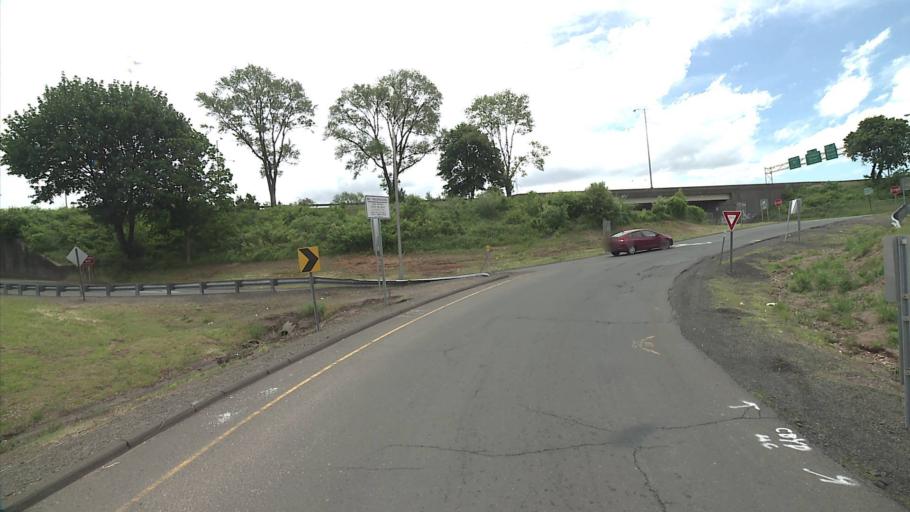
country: US
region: Connecticut
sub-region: New Haven County
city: New Haven
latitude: 41.3191
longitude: -72.9027
